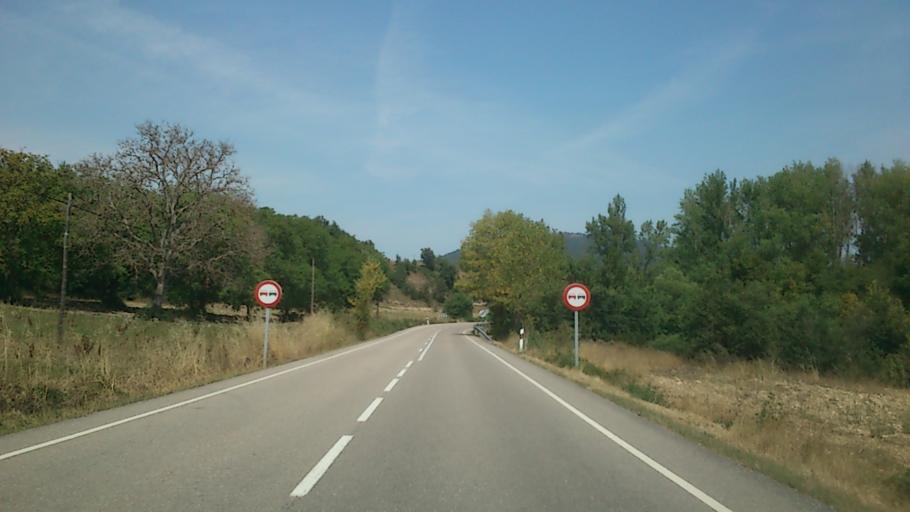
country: ES
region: Castille and Leon
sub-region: Provincia de Burgos
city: Trespaderne
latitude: 42.8604
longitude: -3.3352
